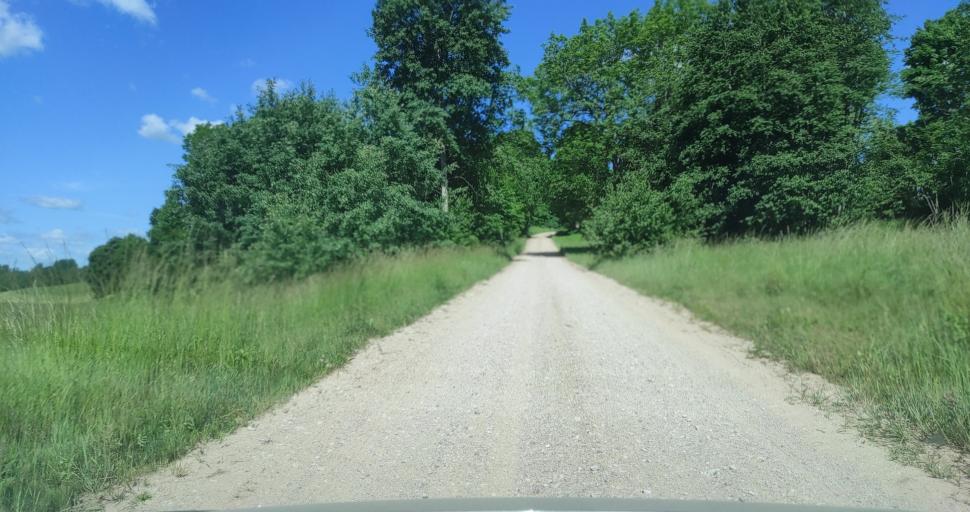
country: LV
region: Kuldigas Rajons
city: Kuldiga
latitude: 56.9351
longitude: 21.8279
